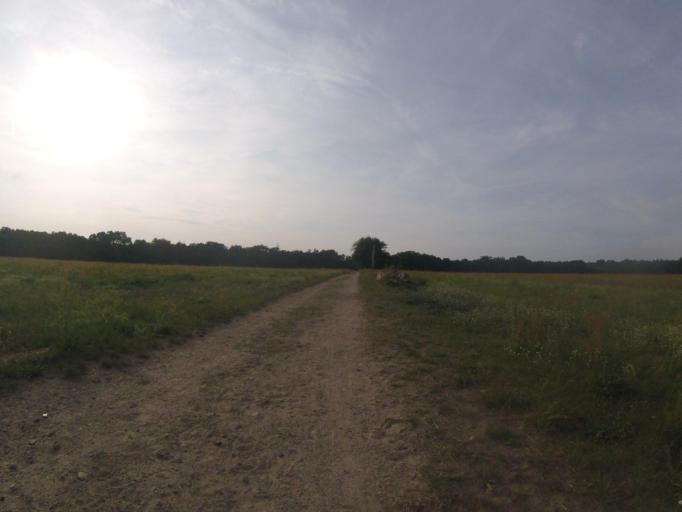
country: DE
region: Brandenburg
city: Schonefeld
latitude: 52.3536
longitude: 13.4594
